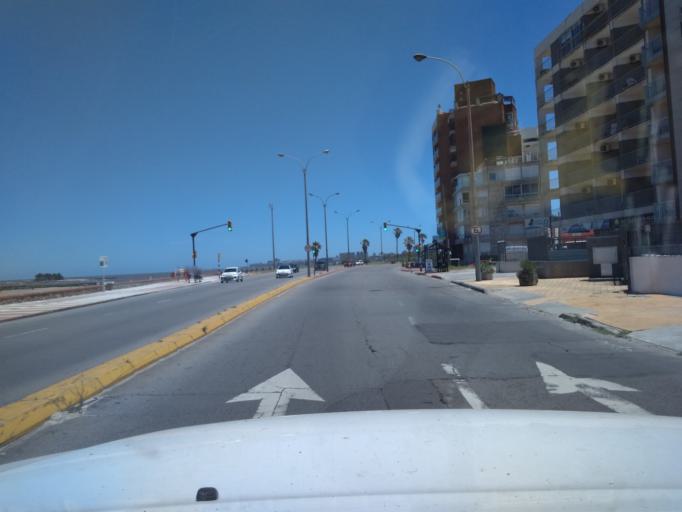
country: UY
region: Canelones
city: Paso de Carrasco
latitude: -34.8970
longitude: -56.0990
